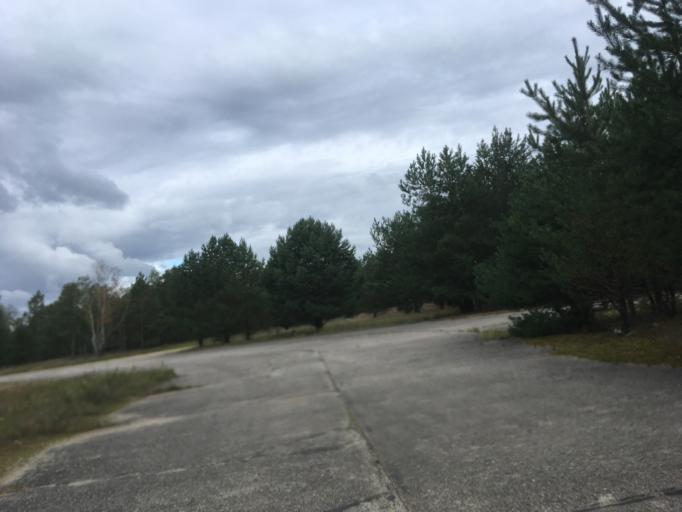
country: DE
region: Brandenburg
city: Halbe
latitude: 52.0385
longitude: 13.7615
